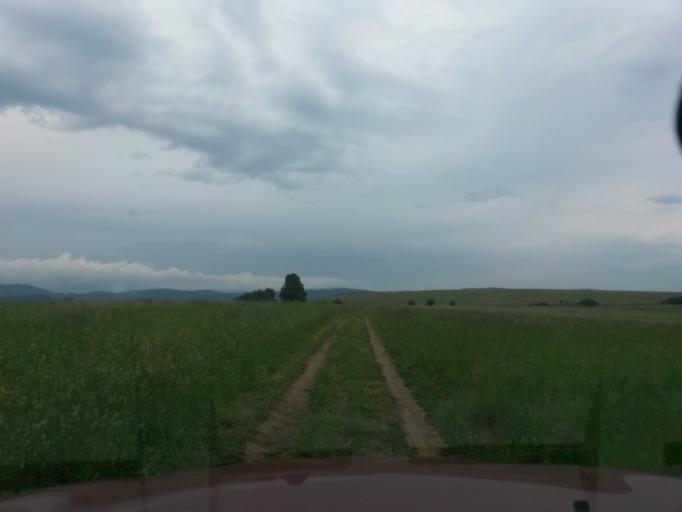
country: SK
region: Kosicky
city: Kosice
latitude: 48.7063
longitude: 21.1620
